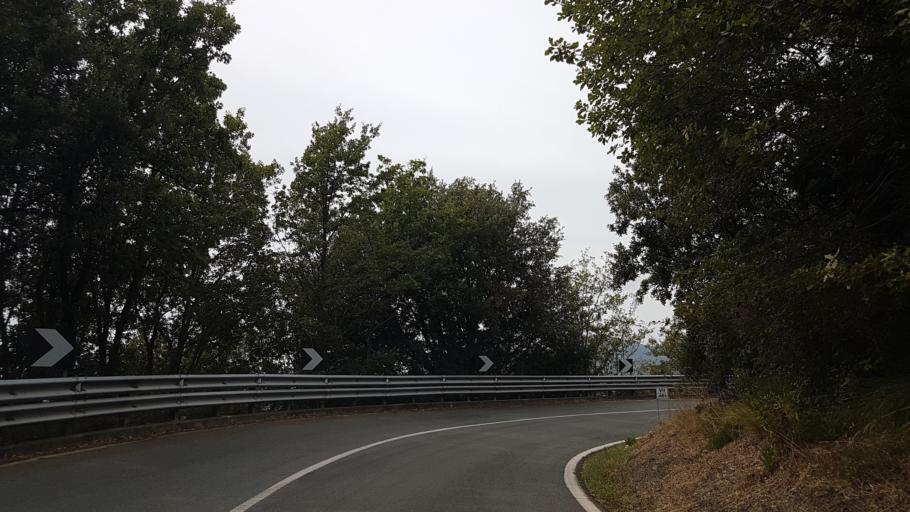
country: IT
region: Liguria
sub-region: Provincia di Genova
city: Castiglione
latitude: 44.2569
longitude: 9.5132
